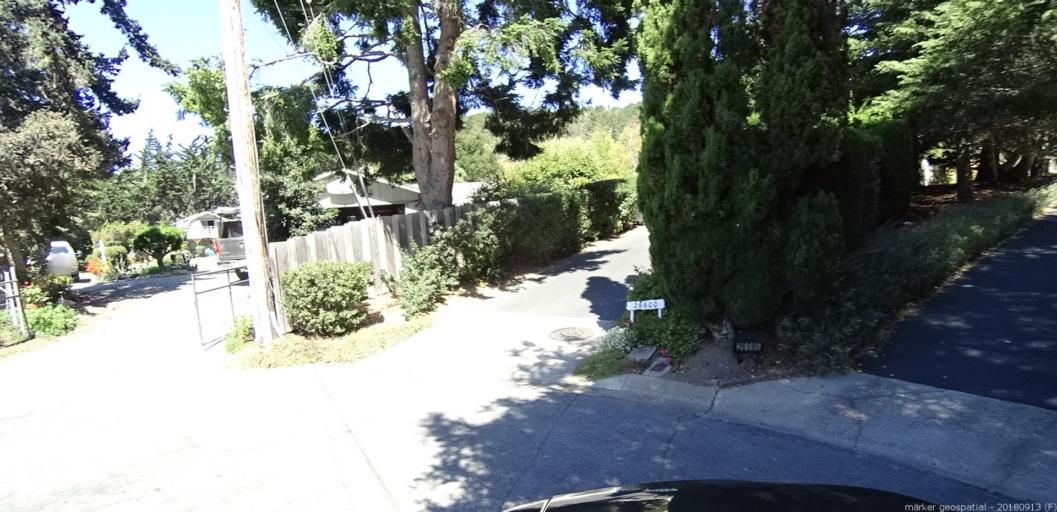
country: US
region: California
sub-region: Monterey County
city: Del Rey Oaks
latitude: 36.5384
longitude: -121.8631
